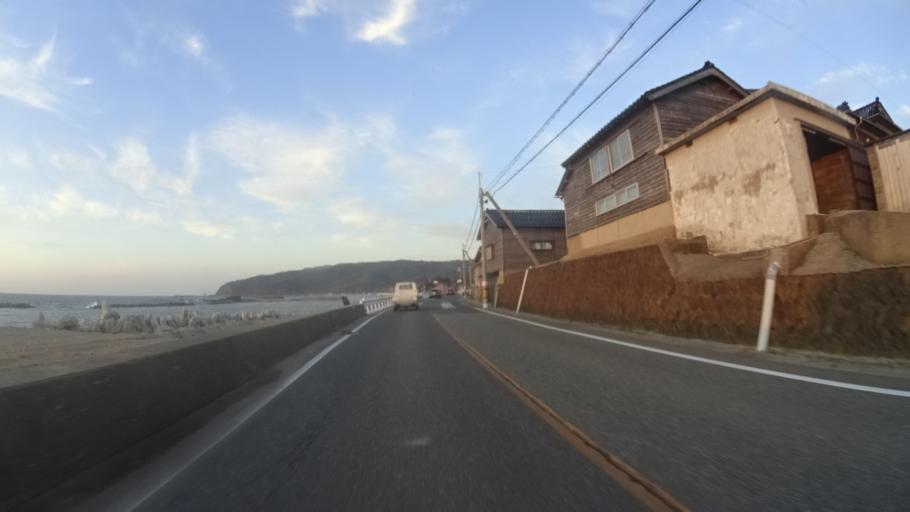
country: JP
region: Ishikawa
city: Nanao
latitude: 37.2772
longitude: 136.7332
